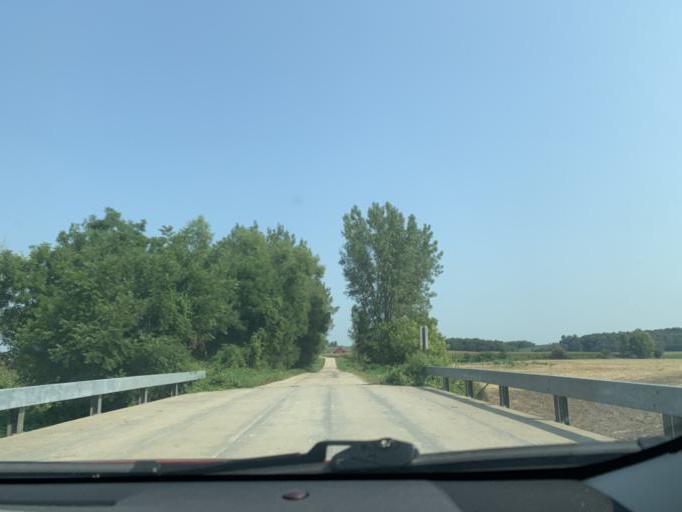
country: US
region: Illinois
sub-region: Whiteside County
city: Morrison
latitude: 41.8652
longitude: -89.8860
